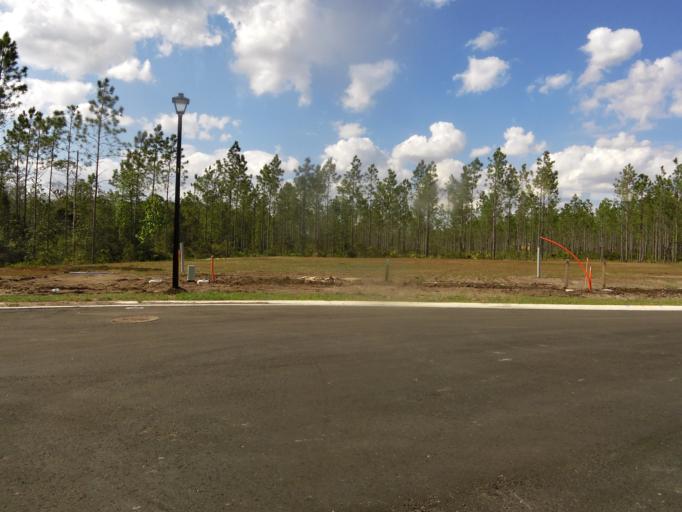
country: US
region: Florida
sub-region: Saint Johns County
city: Palm Valley
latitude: 30.1927
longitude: -81.5084
